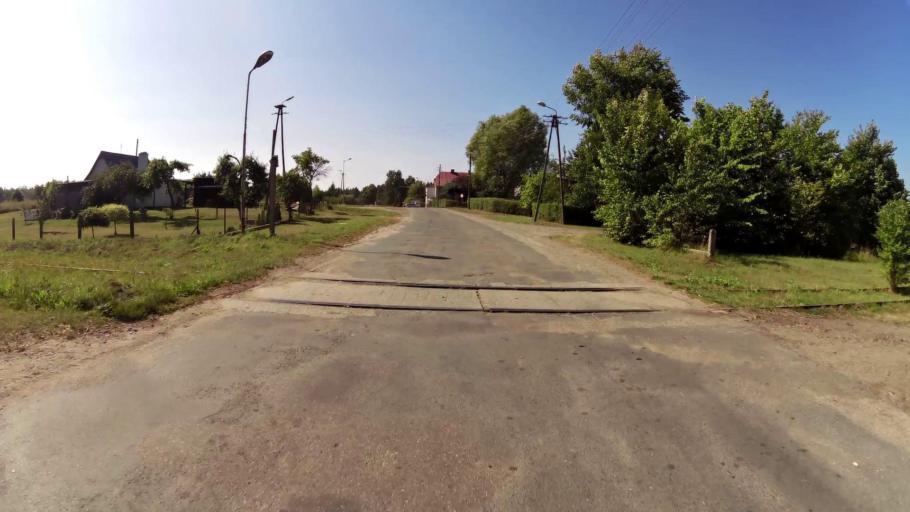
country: PL
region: West Pomeranian Voivodeship
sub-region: Powiat drawski
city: Czaplinek
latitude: 53.4364
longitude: 16.2693
